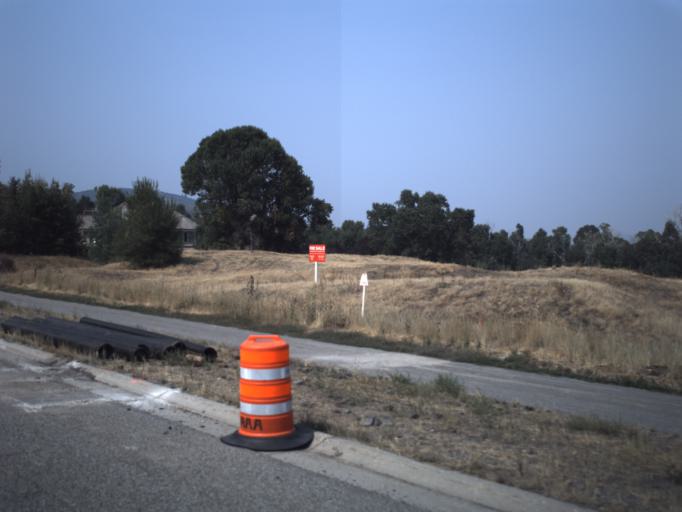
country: US
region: Utah
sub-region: Summit County
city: Snyderville
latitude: 40.6845
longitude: -111.5391
